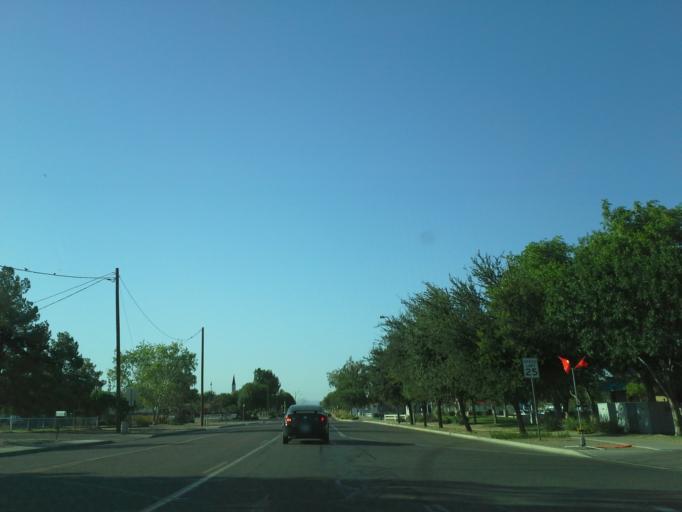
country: US
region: Arizona
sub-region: Maricopa County
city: Queen Creek
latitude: 33.2420
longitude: -111.6345
